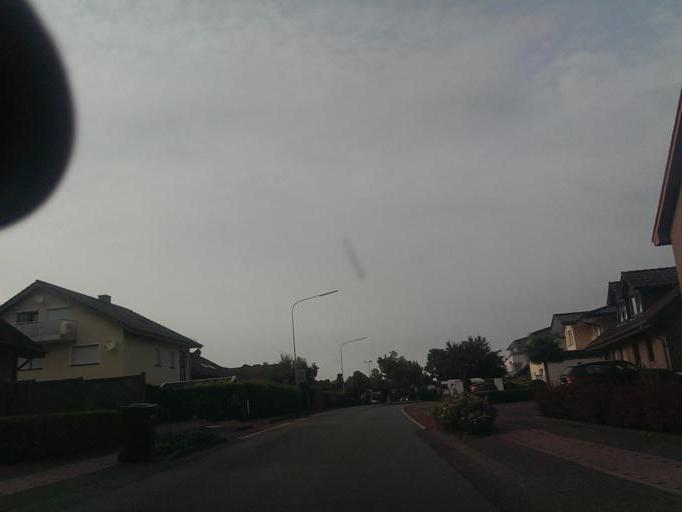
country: DE
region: North Rhine-Westphalia
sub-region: Regierungsbezirk Detmold
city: Delbruck
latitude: 51.7685
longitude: 8.5629
